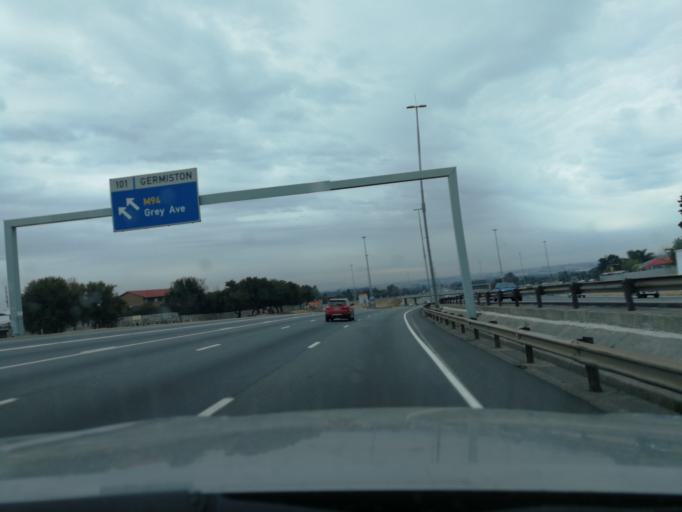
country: ZA
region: Gauteng
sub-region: Ekurhuleni Metropolitan Municipality
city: Germiston
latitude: -26.2616
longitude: 28.1510
